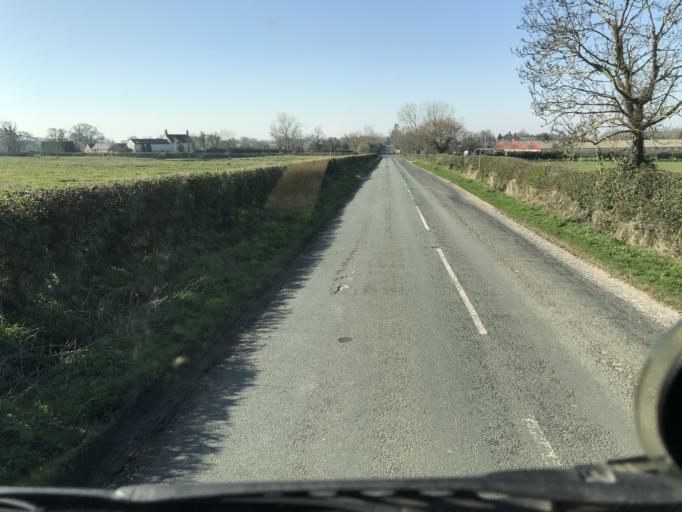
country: GB
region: England
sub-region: Cheshire West and Chester
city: Waverton
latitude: 53.1686
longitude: -2.8216
